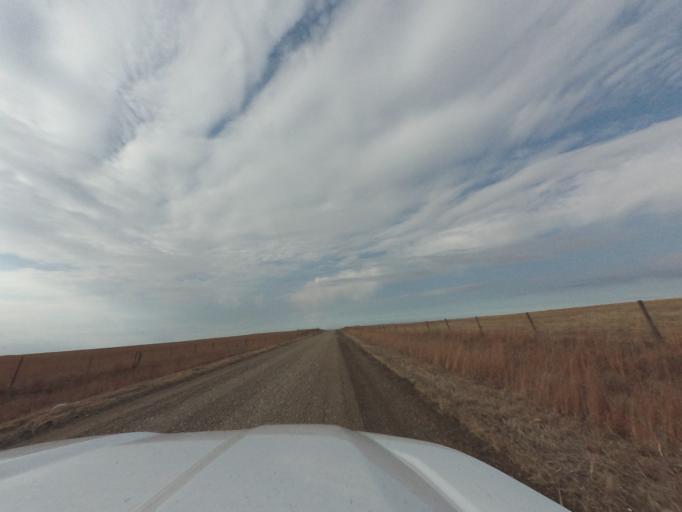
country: US
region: Kansas
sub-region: Chase County
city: Cottonwood Falls
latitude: 38.2171
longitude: -96.6988
